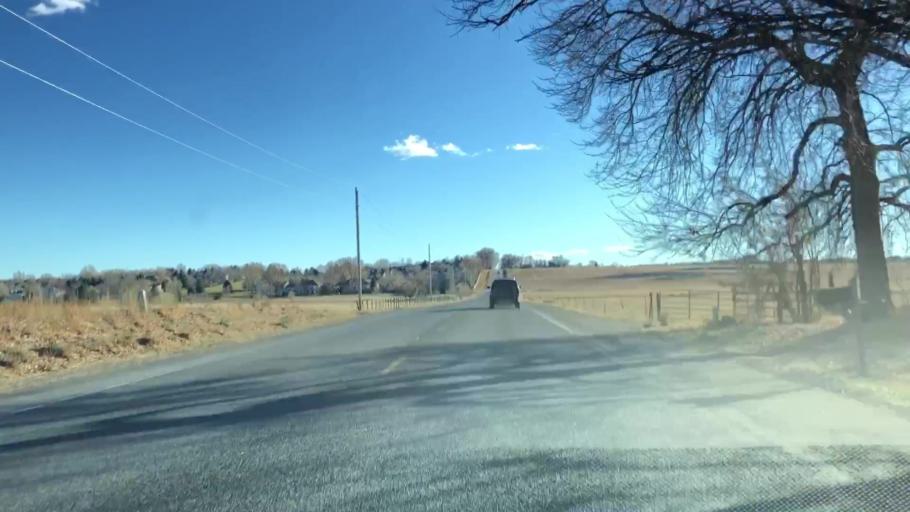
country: US
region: Colorado
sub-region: Weld County
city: Windsor
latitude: 40.4906
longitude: -104.9820
